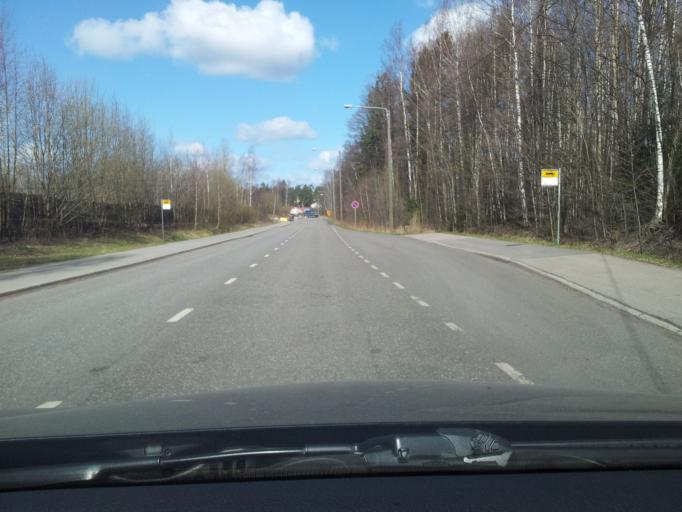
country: FI
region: Uusimaa
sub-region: Helsinki
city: Koukkuniemi
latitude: 60.1505
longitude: 24.7096
